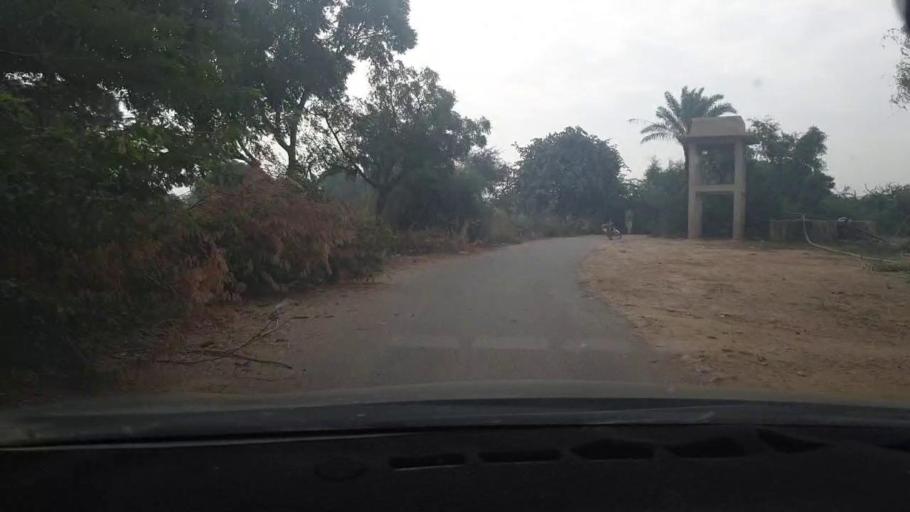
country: PK
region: Sindh
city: Malir Cantonment
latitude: 24.9548
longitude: 67.4106
